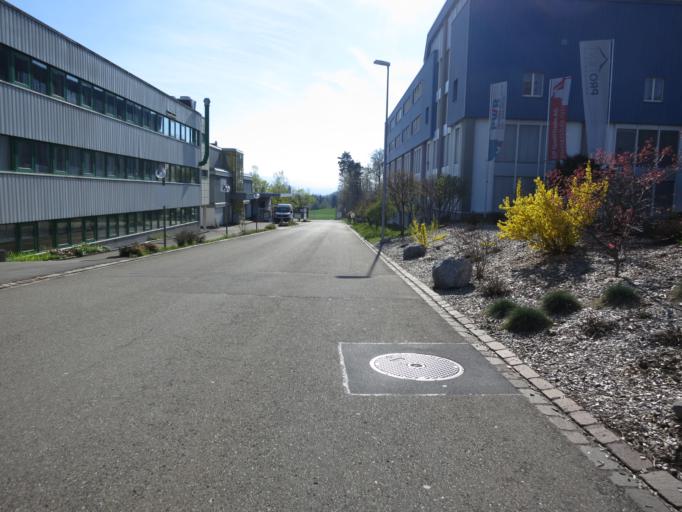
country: CH
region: Zurich
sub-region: Bezirk Hinwil
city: Rueti / Oberdorf
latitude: 47.2675
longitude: 8.8675
